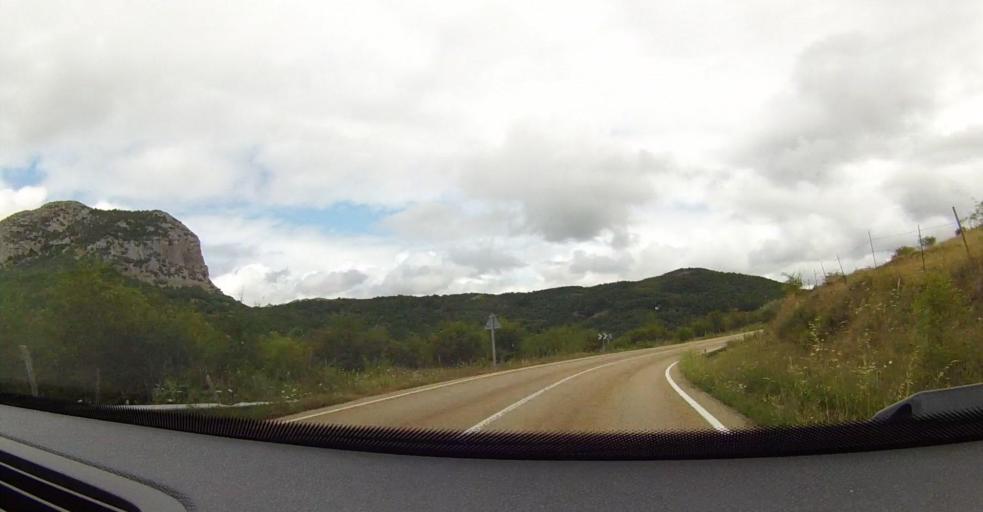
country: ES
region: Castille and Leon
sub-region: Provincia de Leon
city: Reyero
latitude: 42.9432
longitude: -5.2592
